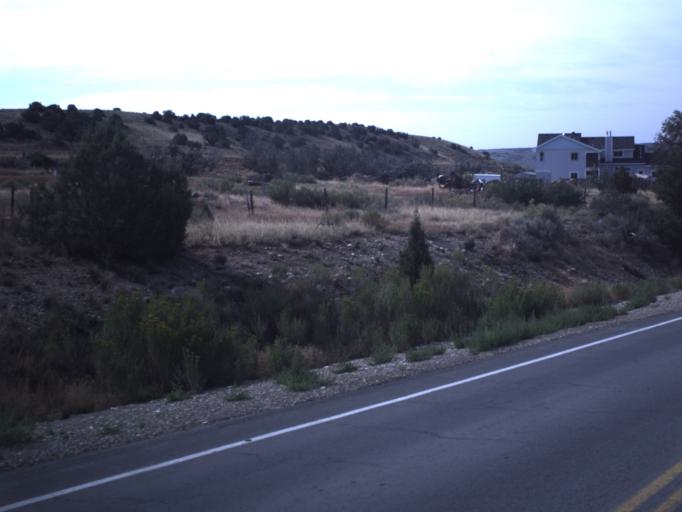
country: US
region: Utah
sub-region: Duchesne County
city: Duchesne
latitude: 40.1779
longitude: -110.4002
